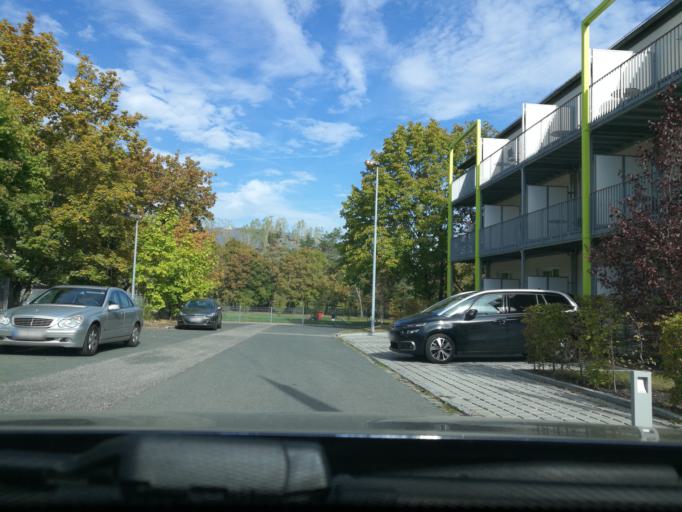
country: DE
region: Bavaria
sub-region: Regierungsbezirk Mittelfranken
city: Furth
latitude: 49.5061
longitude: 10.9626
